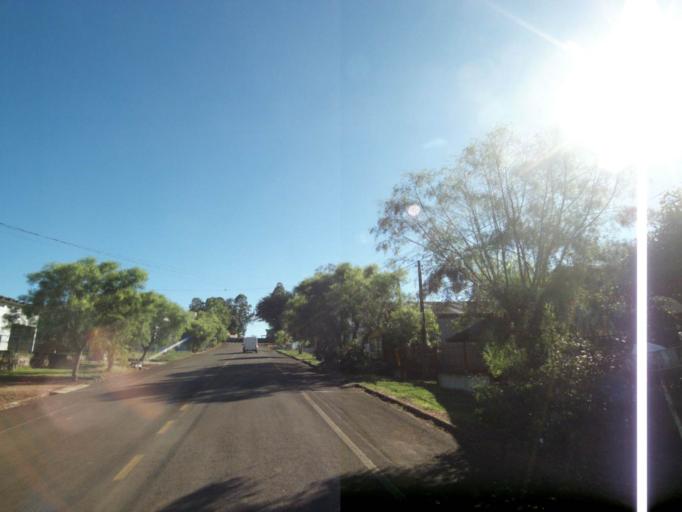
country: BR
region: Parana
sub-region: Pato Branco
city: Pato Branco
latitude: -26.2600
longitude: -52.7763
